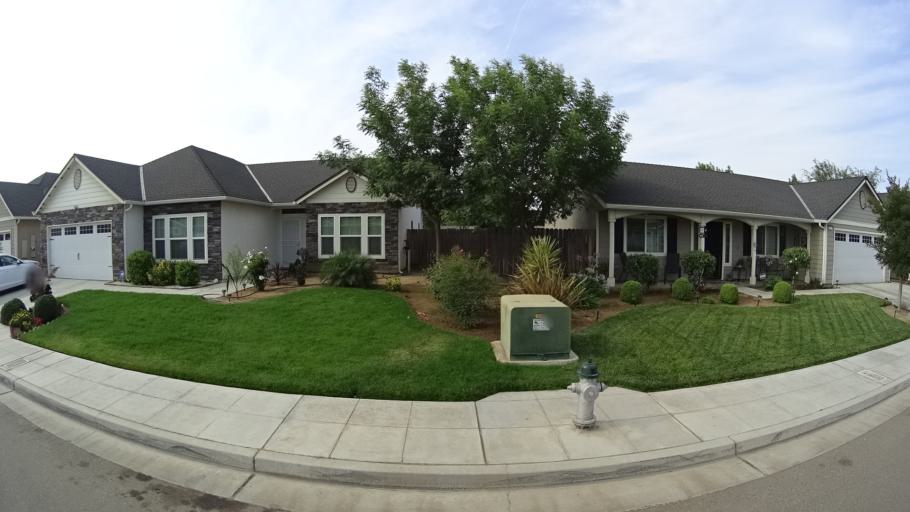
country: US
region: California
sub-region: Fresno County
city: West Park
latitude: 36.7740
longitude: -119.8773
